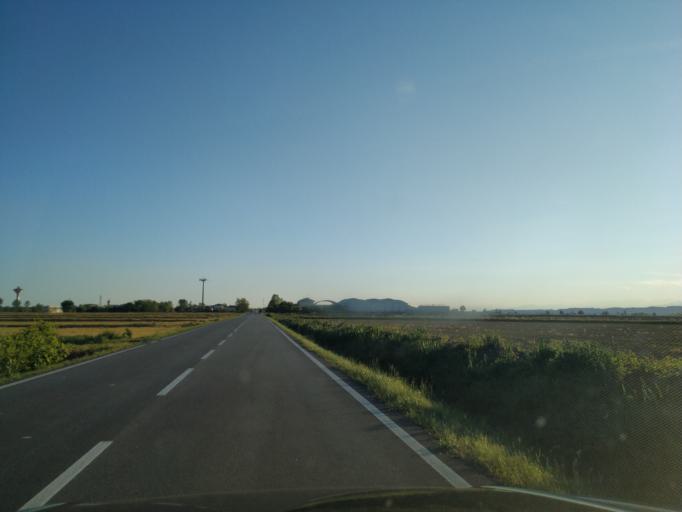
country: IT
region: Piedmont
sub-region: Provincia di Vercelli
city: Buronzo
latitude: 45.4517
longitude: 8.2391
